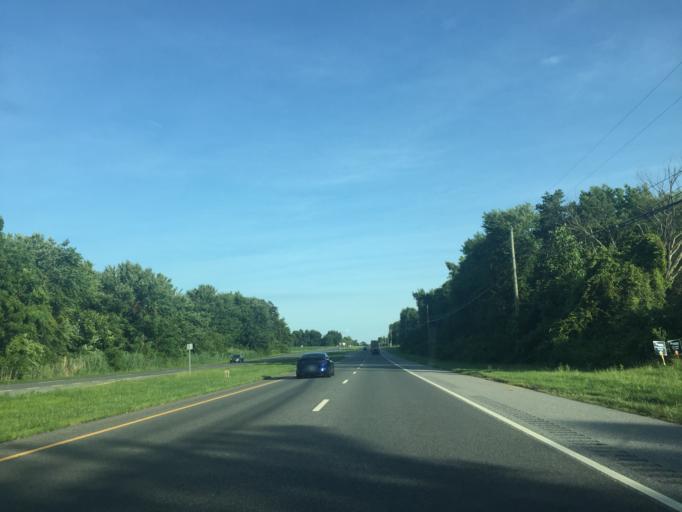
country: US
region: Delaware
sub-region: Kent County
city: Cheswold
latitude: 39.2396
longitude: -75.5854
